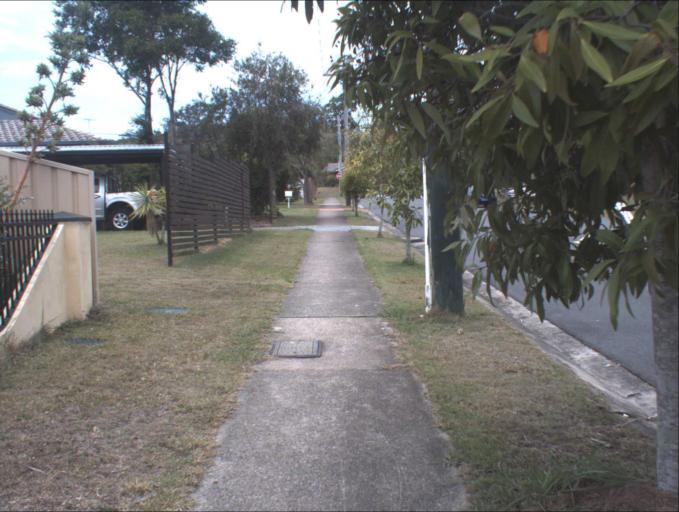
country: AU
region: Queensland
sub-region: Logan
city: Springwood
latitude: -27.6263
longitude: 153.1359
